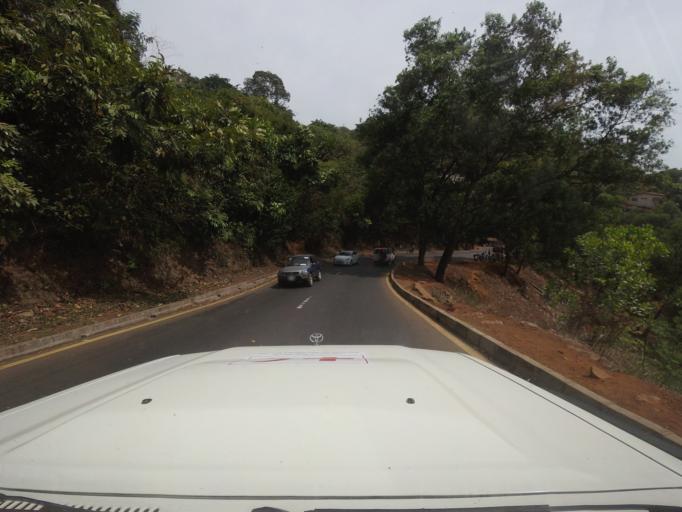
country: SL
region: Western Area
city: Freetown
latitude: 8.4791
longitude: -13.2245
